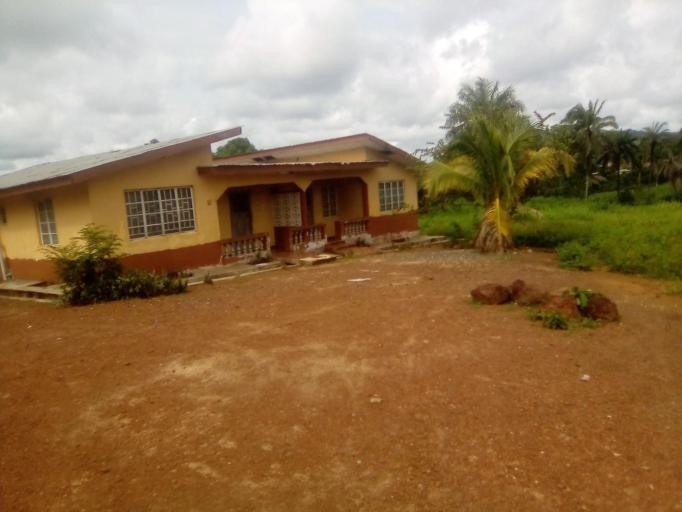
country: SL
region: Southern Province
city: Moyamba
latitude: 8.1468
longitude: -12.4341
